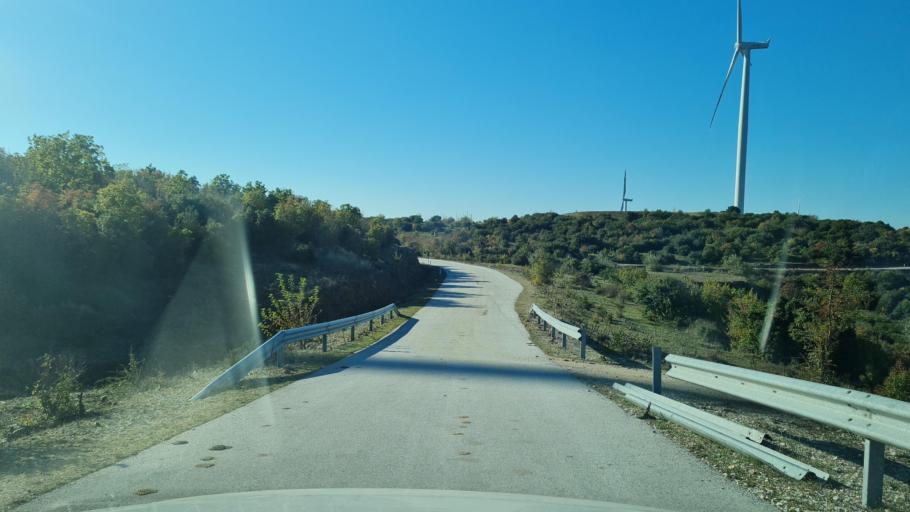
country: MK
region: Bogdanci
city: Bogdanci
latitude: 41.2240
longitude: 22.5516
